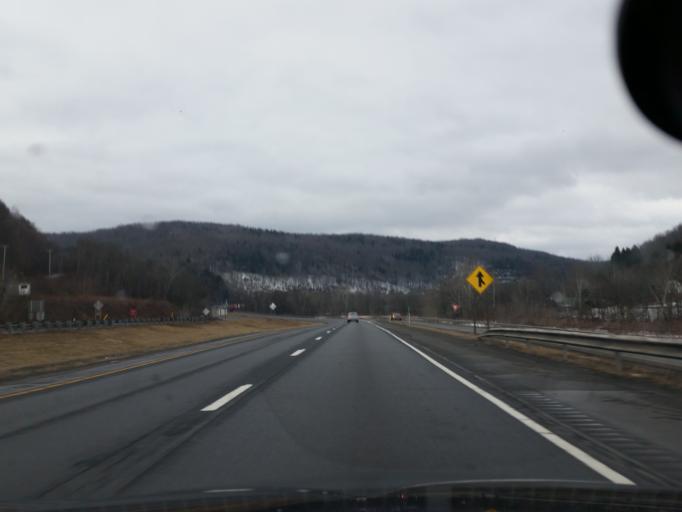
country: US
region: Pennsylvania
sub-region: Wyoming County
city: Factoryville
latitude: 41.7087
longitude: -75.6707
